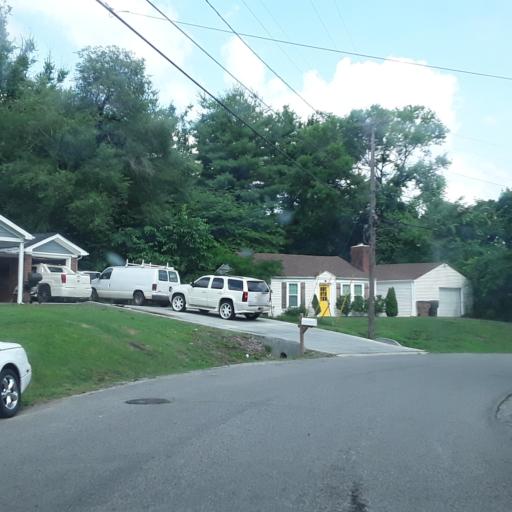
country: US
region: Tennessee
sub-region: Davidson County
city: Oak Hill
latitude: 36.1113
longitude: -86.7340
